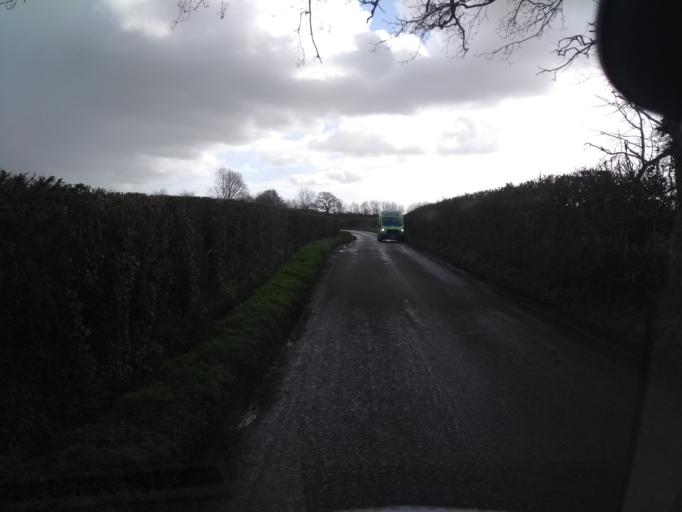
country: GB
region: England
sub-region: Somerset
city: Martock
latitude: 50.9780
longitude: -2.7755
